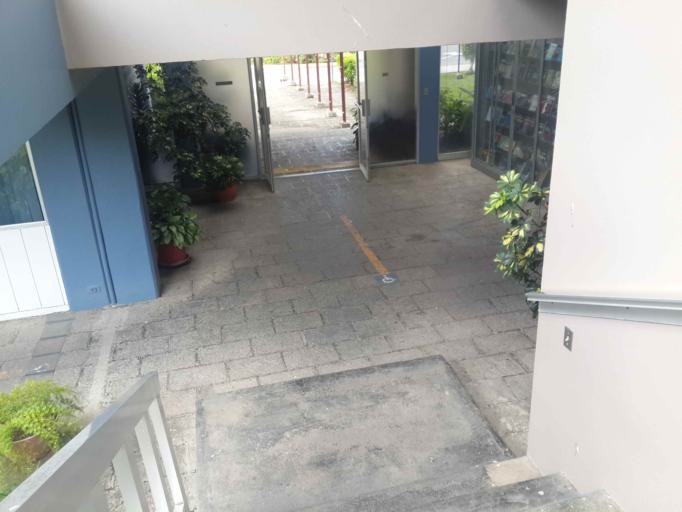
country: CR
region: Cartago
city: Cartago
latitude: 9.8569
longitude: -83.9124
